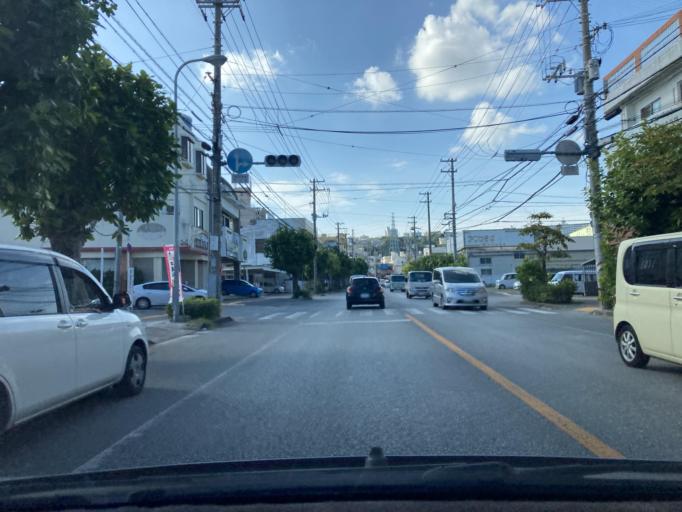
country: JP
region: Okinawa
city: Okinawa
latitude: 26.3242
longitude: 127.8258
